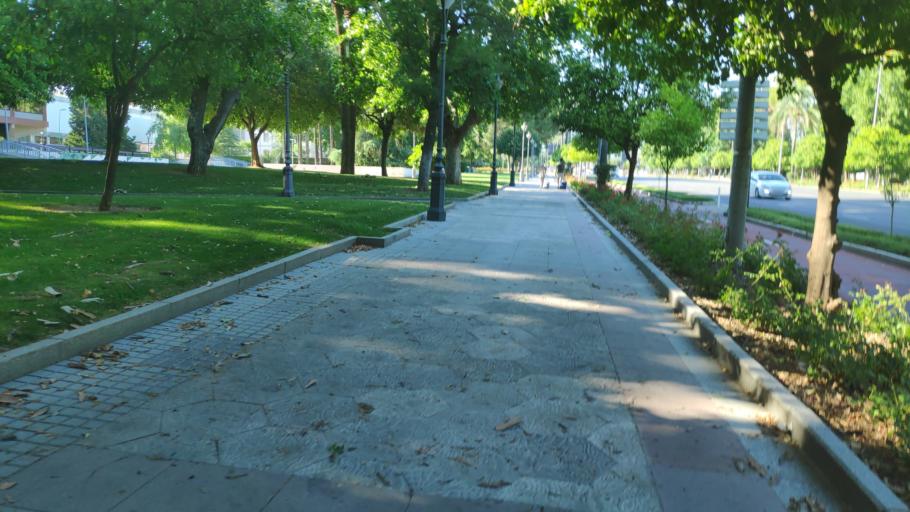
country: ES
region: Andalusia
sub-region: Province of Cordoba
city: Cordoba
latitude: 37.8772
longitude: -4.7863
